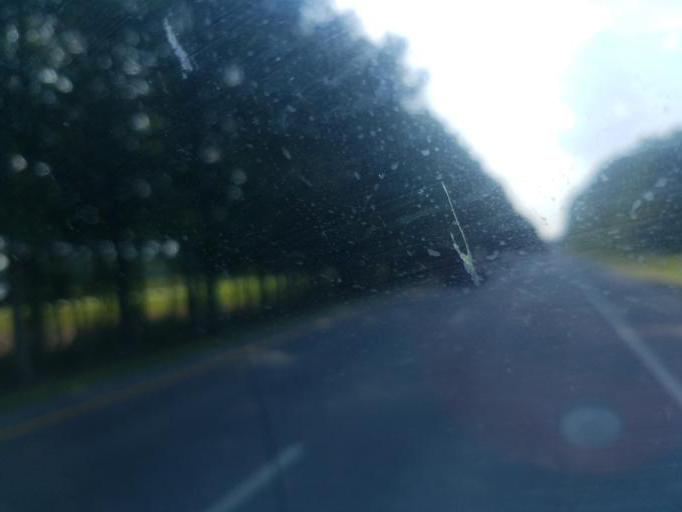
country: US
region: Maryland
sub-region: Worcester County
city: Berlin
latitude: 38.3669
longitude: -75.2663
